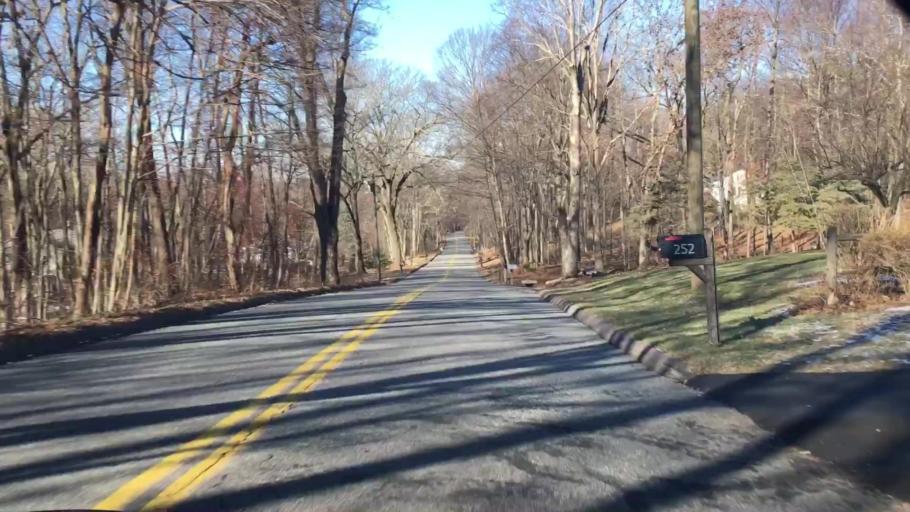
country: US
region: Connecticut
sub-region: Tolland County
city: Tolland
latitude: 41.8914
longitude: -72.3878
